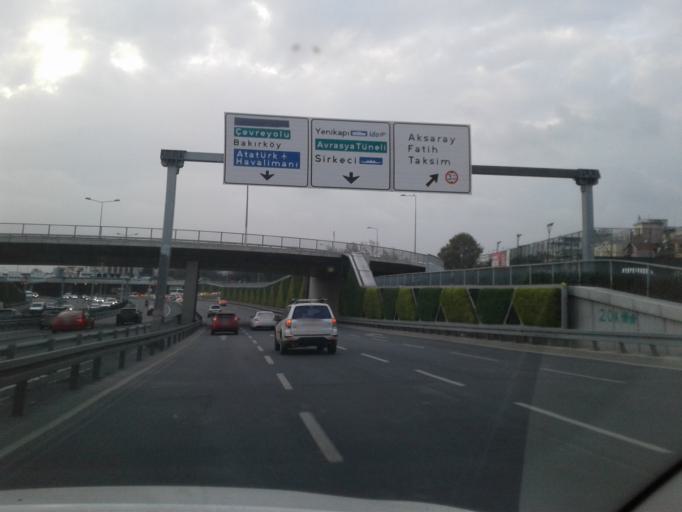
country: TR
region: Istanbul
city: Istanbul
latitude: 41.0038
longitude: 28.9578
